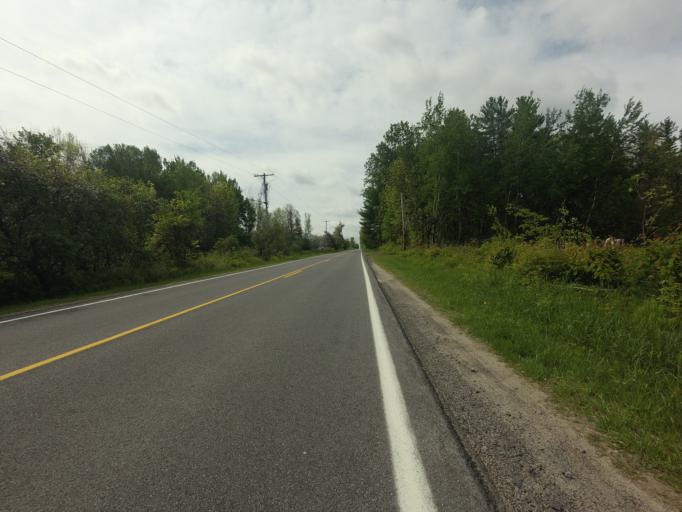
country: CA
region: Ontario
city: Cornwall
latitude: 44.7404
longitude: -74.6663
